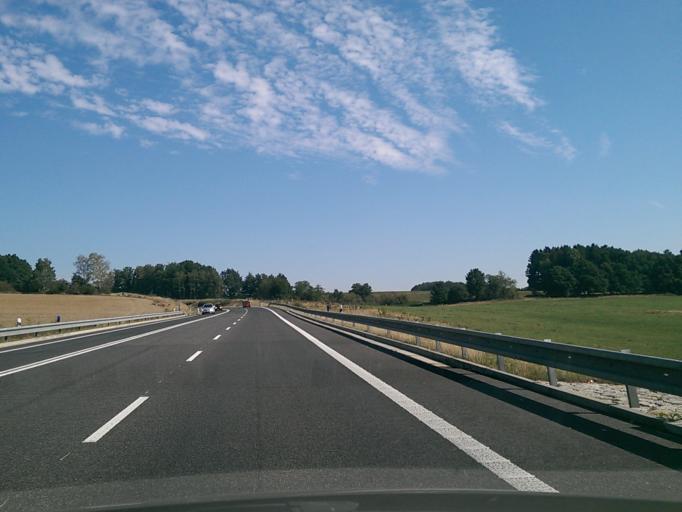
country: CZ
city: Chrastava
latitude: 50.8298
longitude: 14.9390
